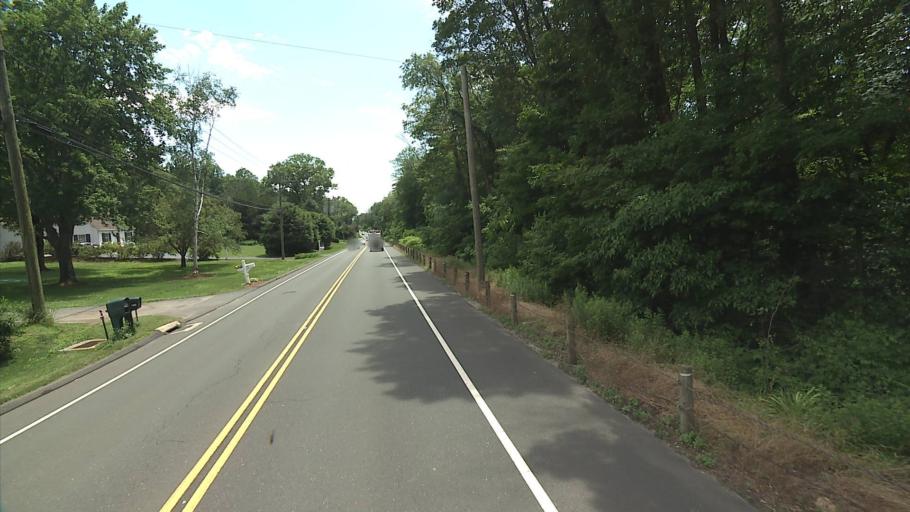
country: US
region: Connecticut
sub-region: New Haven County
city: Waterbury
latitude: 41.5503
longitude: -73.0916
